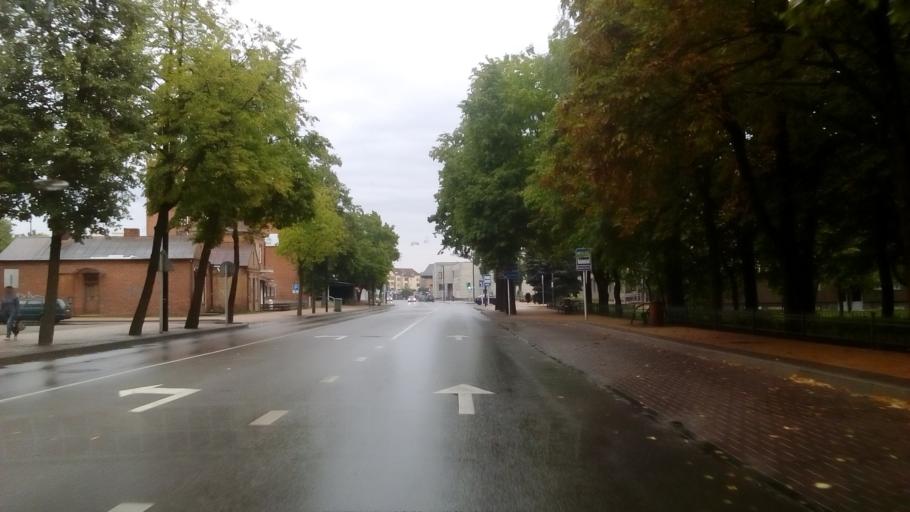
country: LT
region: Alytaus apskritis
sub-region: Alytus
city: Alytus
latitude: 54.3944
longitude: 24.0456
